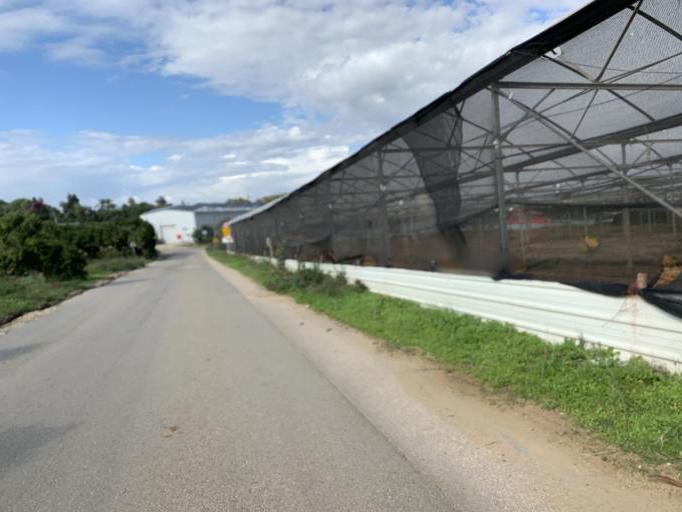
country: IL
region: Central District
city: Ra'anana
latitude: 32.1687
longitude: 34.8786
